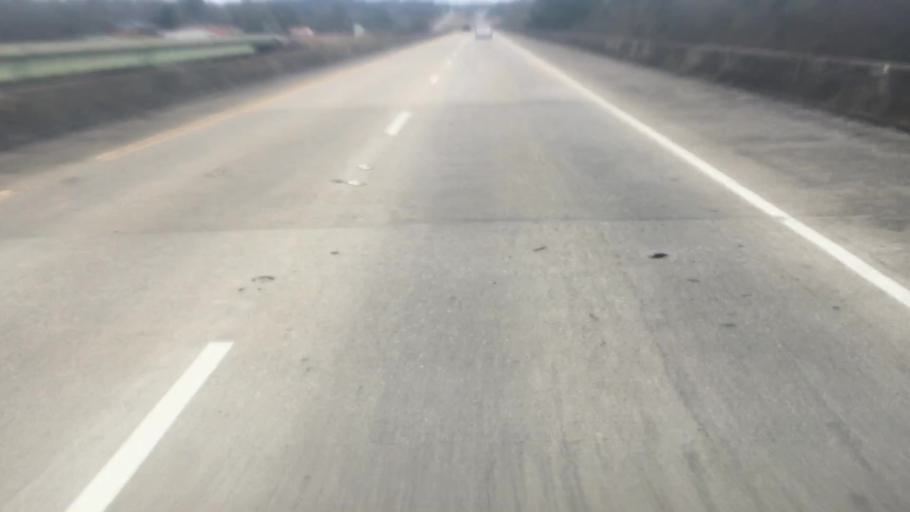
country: US
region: Alabama
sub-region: Walker County
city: Cordova
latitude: 33.8067
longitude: -87.1416
